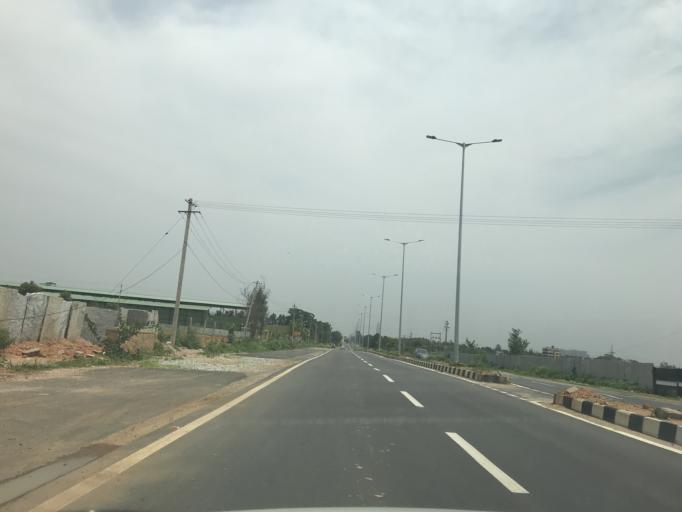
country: IN
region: Karnataka
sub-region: Bangalore Urban
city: Yelahanka
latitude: 13.1145
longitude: 77.6680
